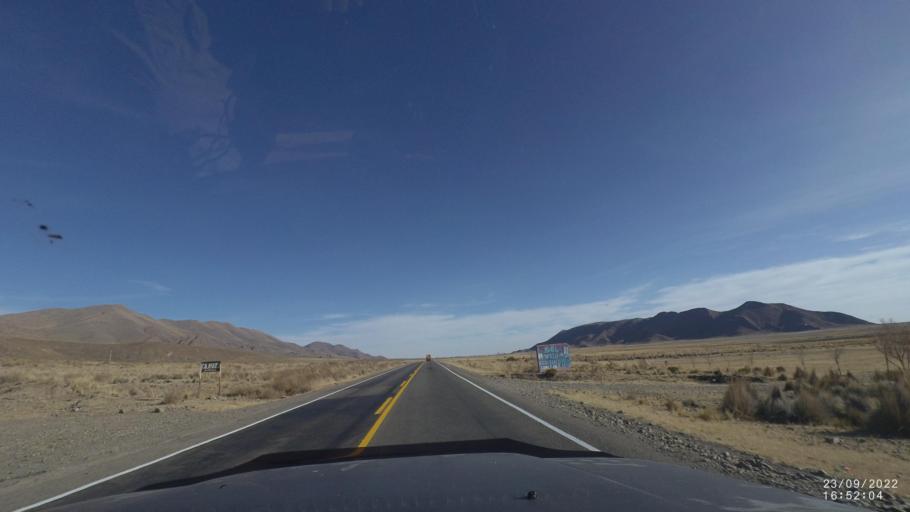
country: BO
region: Oruro
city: Poopo
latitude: -18.4255
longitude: -66.9742
